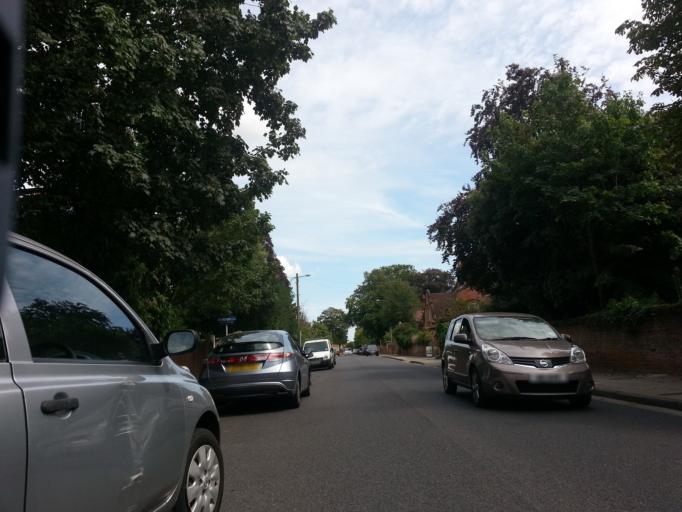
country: GB
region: England
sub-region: Suffolk
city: Ipswich
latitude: 52.0677
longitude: 1.1558
